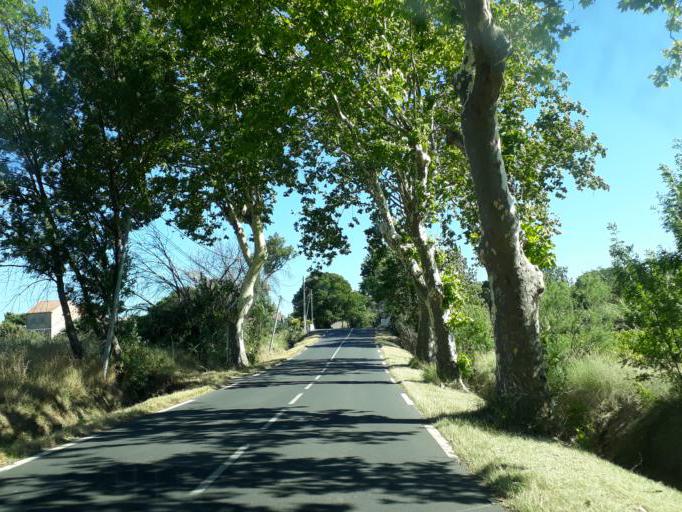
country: FR
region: Languedoc-Roussillon
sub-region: Departement de l'Herault
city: Florensac
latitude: 43.3884
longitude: 3.4620
